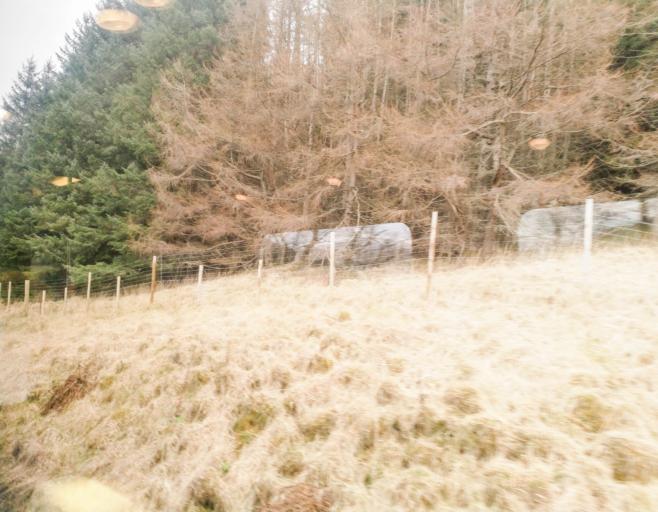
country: GB
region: Scotland
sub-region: Argyll and Bute
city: Garelochhead
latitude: 56.4382
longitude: -4.7064
